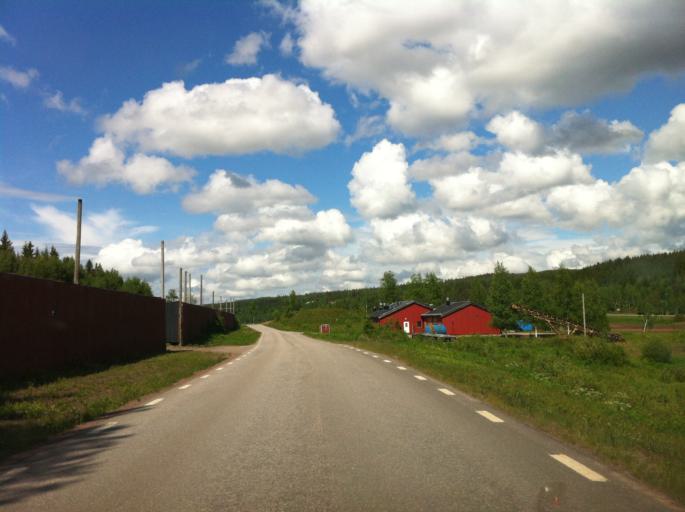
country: SE
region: Dalarna
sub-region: Malung-Saelens kommun
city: Malung
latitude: 61.1360
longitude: 13.2728
